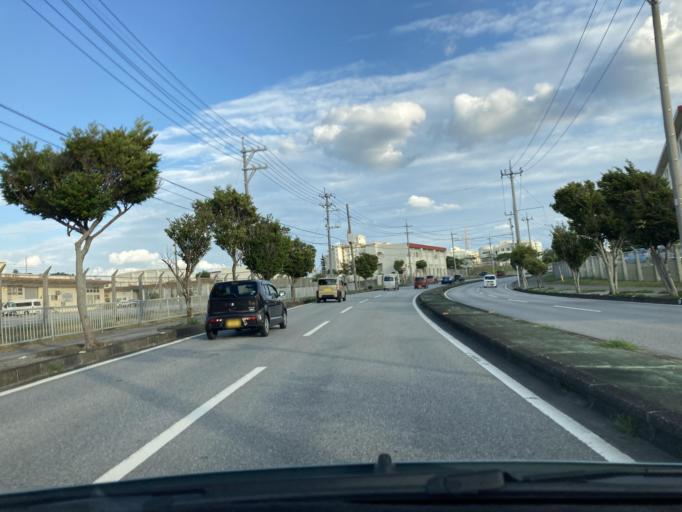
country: JP
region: Okinawa
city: Chatan
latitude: 26.3076
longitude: 127.7690
